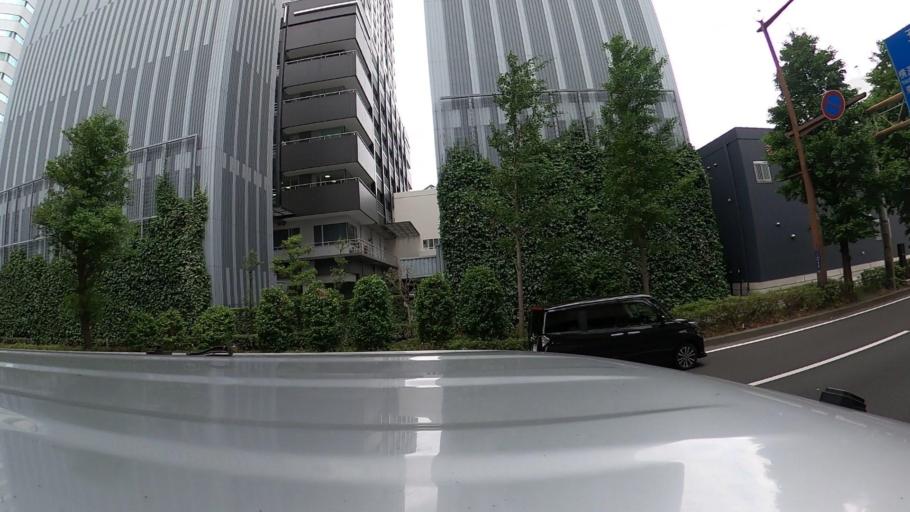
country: JP
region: Kanagawa
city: Yokohama
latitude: 35.4626
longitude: 139.6251
